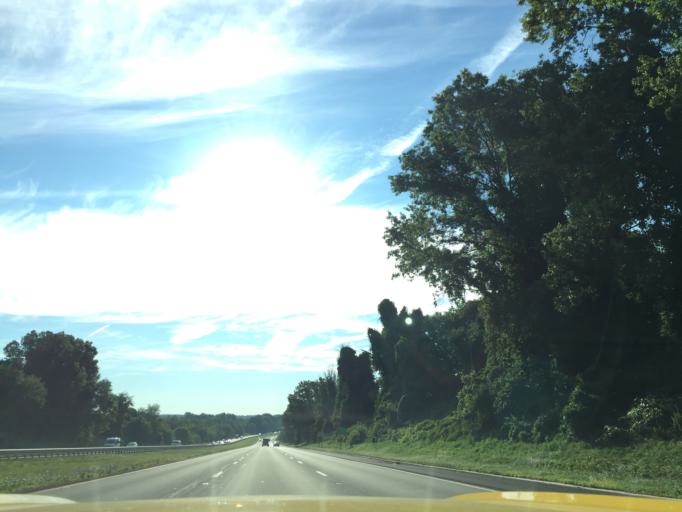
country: US
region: New Jersey
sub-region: Hunterdon County
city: Lebanon
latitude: 40.6465
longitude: -74.8483
